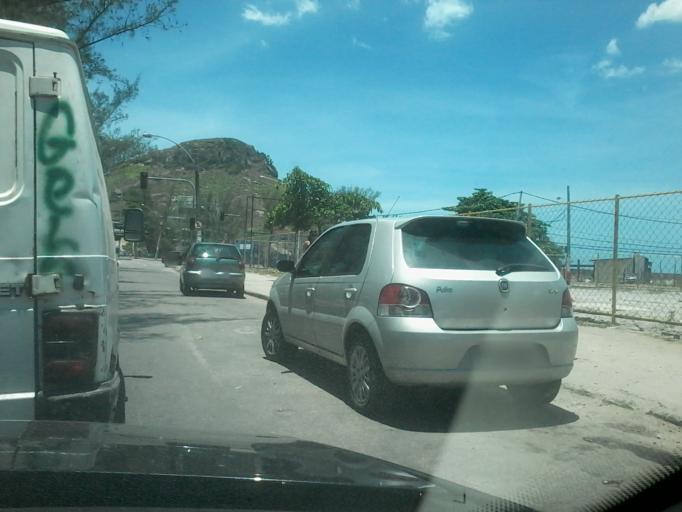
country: BR
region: Rio de Janeiro
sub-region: Nilopolis
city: Nilopolis
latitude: -23.0304
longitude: -43.4722
